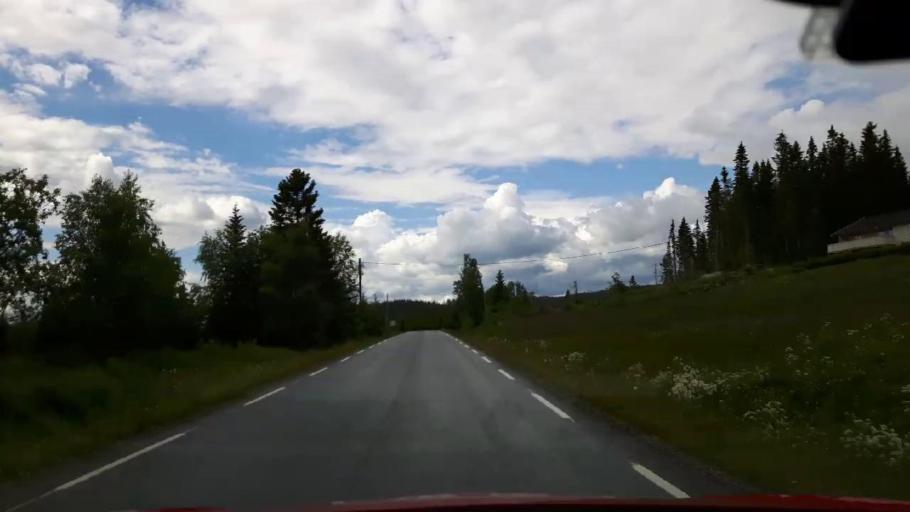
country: NO
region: Nord-Trondelag
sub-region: Lierne
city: Sandvika
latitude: 64.0961
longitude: 14.0377
